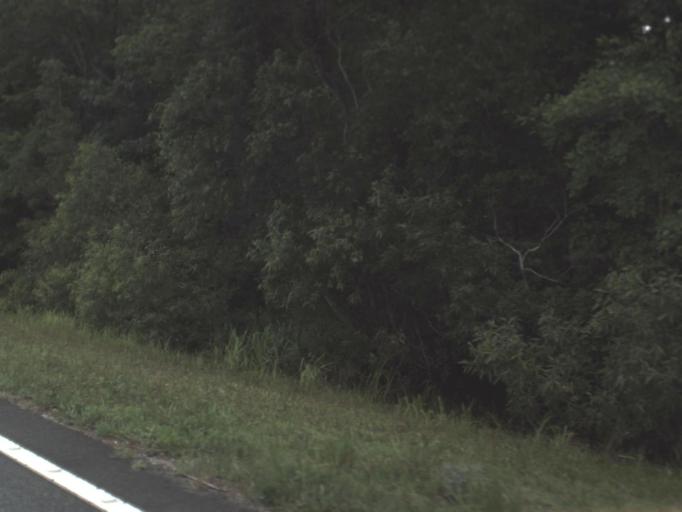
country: US
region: Florida
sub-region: Levy County
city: Chiefland
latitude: 29.3015
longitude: -82.8140
